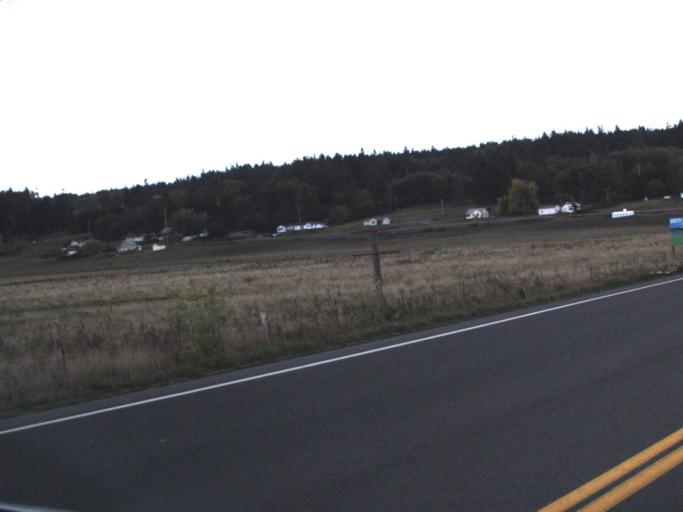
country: US
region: Washington
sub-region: Island County
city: Ault Field
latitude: 48.3526
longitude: -122.6124
